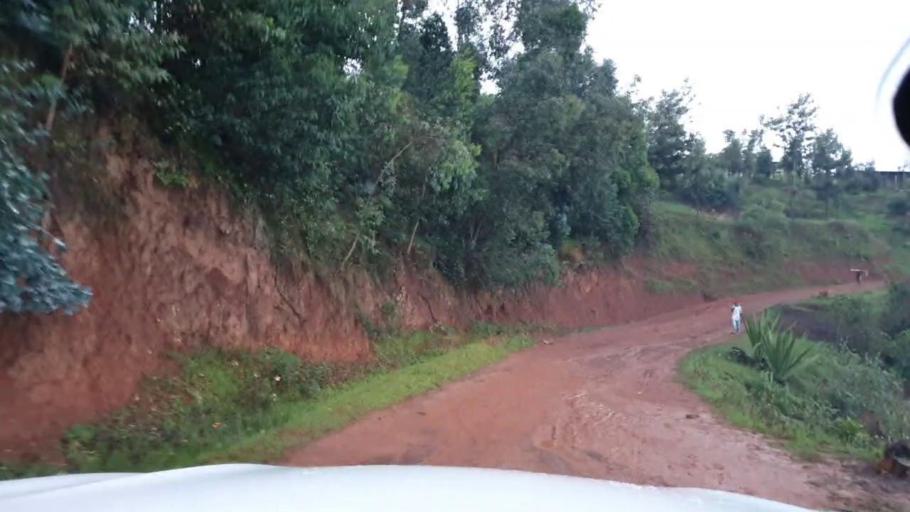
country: BI
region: Kayanza
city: Kayanza
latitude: -2.7144
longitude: 29.5409
